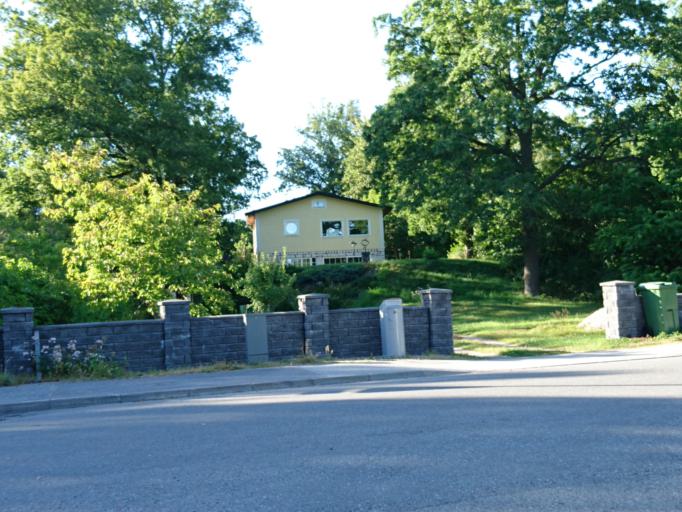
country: SE
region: Stockholm
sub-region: Huddinge Kommun
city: Segeltorp
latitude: 59.2750
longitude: 17.9345
